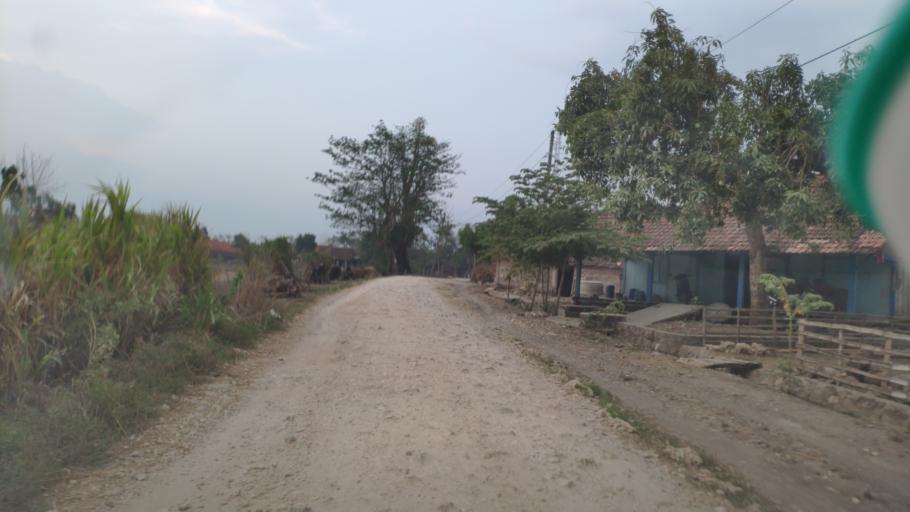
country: ID
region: Central Java
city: Kadengan
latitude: -7.1593
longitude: 111.3737
